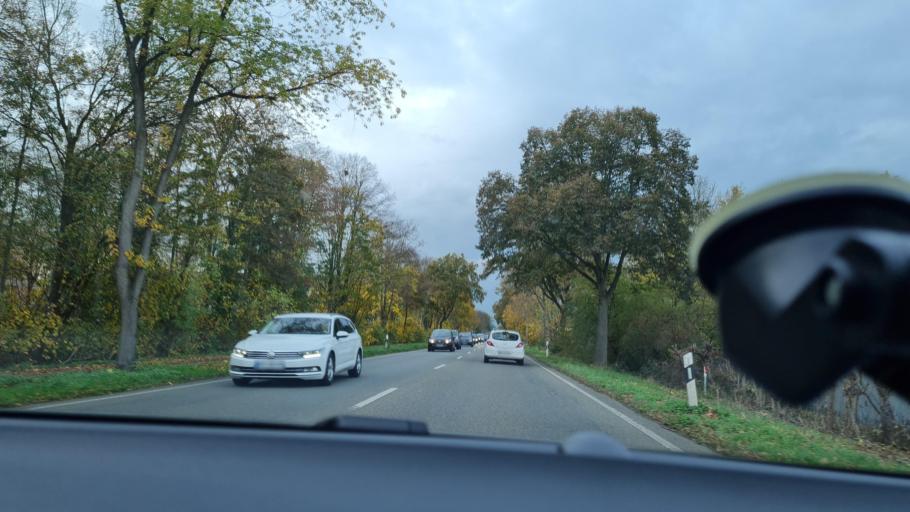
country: DE
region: North Rhine-Westphalia
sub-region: Regierungsbezirk Dusseldorf
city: Voerde
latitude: 51.6271
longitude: 6.6634
